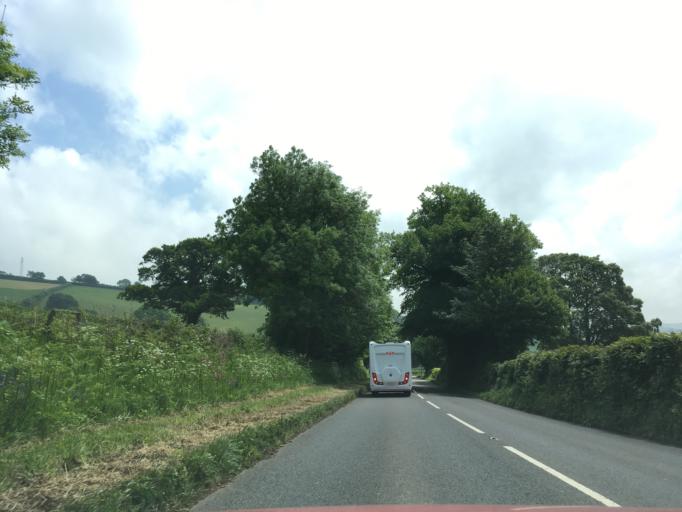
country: GB
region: England
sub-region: Devon
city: Totnes
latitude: 50.4044
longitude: -3.7125
